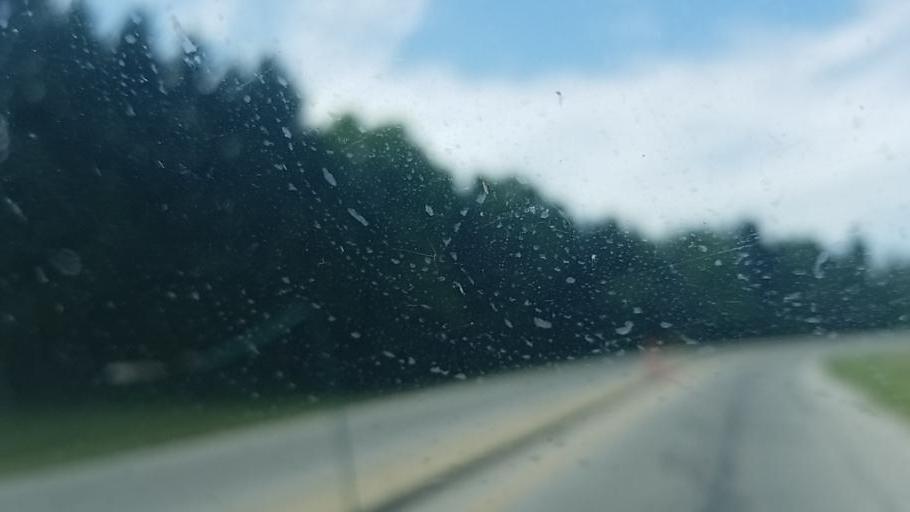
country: US
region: Ohio
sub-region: Richland County
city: Ontario
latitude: 40.7693
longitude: -82.5825
